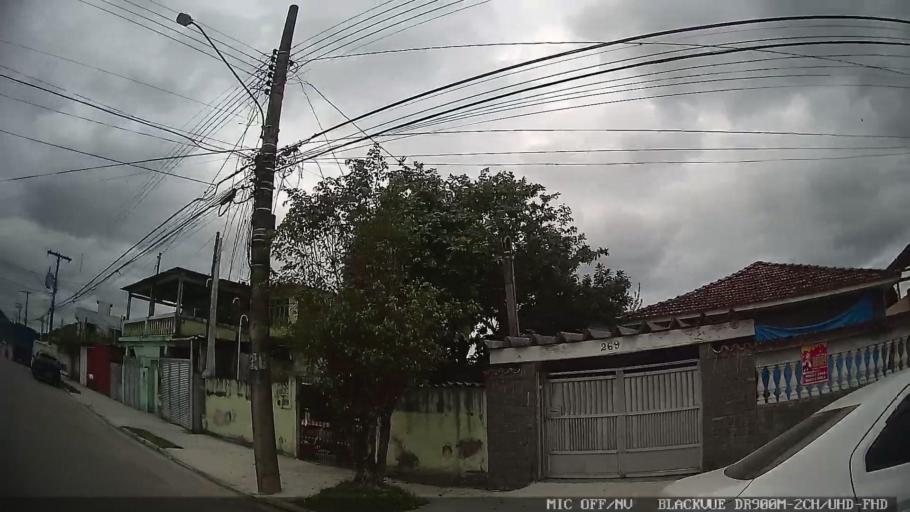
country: BR
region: Sao Paulo
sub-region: Guaruja
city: Guaruja
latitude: -23.9973
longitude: -46.2878
